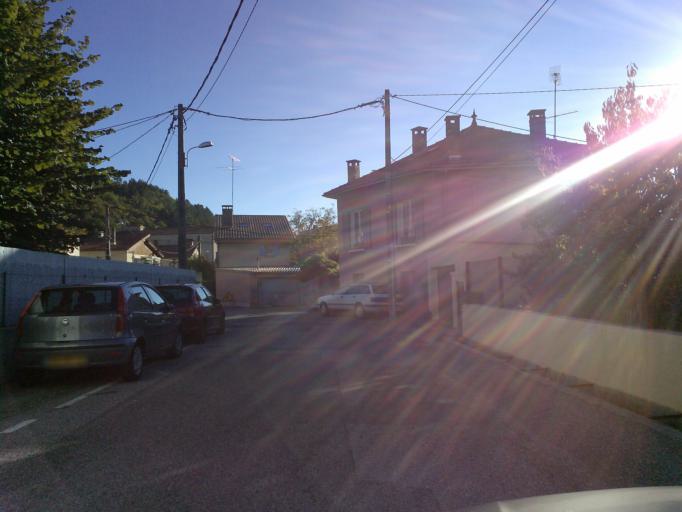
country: FR
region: Provence-Alpes-Cote d'Azur
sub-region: Departement des Alpes-de-Haute-Provence
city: Digne-les-Bains
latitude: 44.0883
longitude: 6.2303
